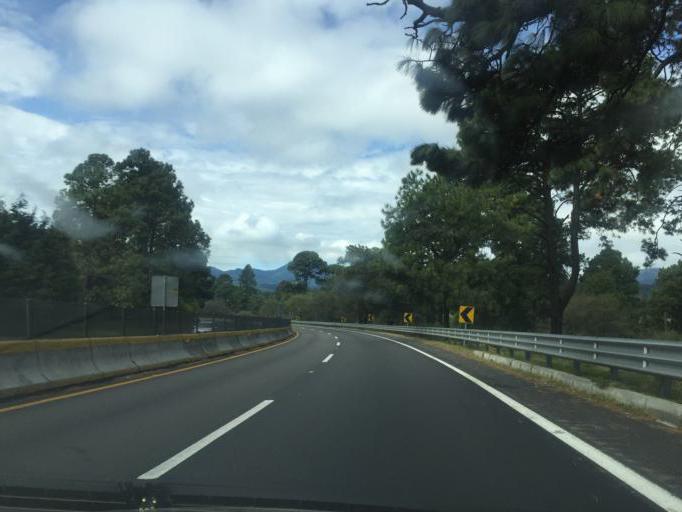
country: MX
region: Morelos
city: Tres Marias
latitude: 19.0838
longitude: -99.2292
